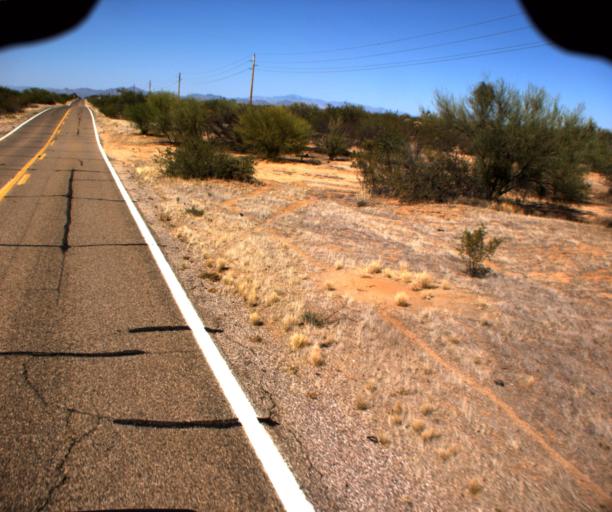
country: US
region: Arizona
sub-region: Pima County
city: Three Points
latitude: 32.0286
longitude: -111.3430
